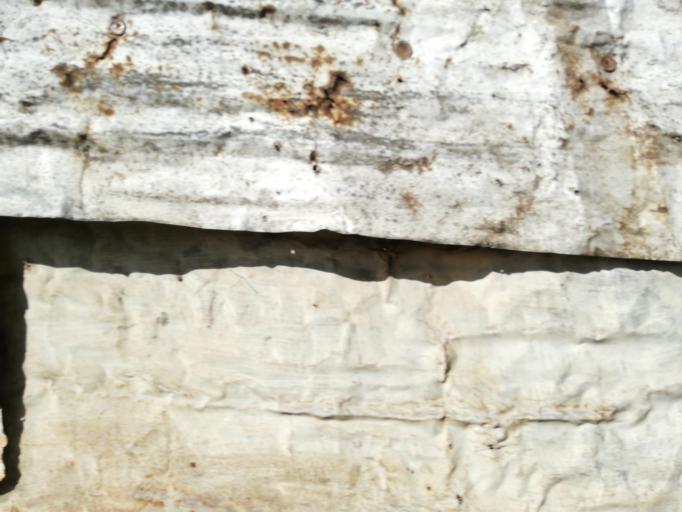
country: MU
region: Port Louis
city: Port Louis
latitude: -20.1665
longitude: 57.4831
